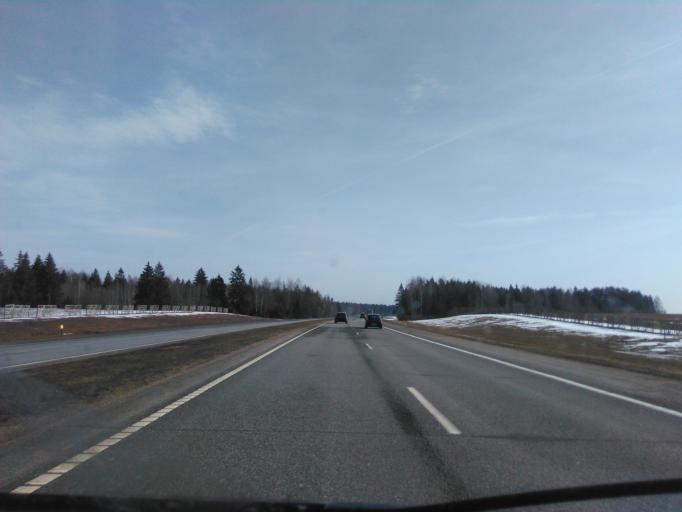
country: BY
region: Vitebsk
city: Talachyn
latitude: 54.4792
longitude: 29.8382
